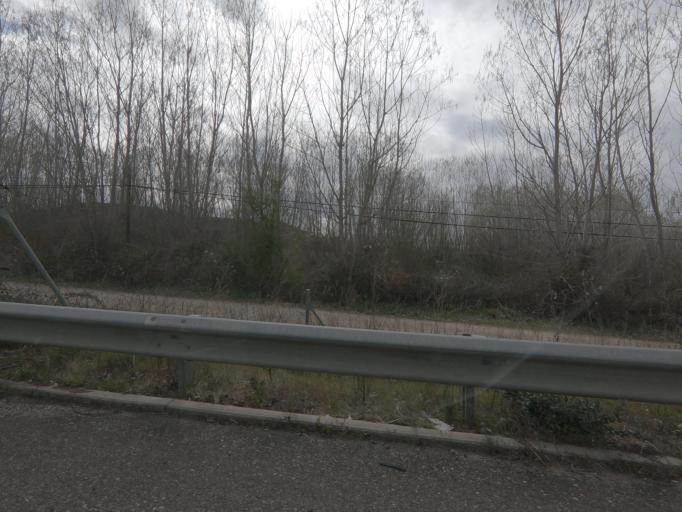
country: ES
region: Castille and Leon
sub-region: Provincia de Salamanca
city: Ciudad Rodrigo
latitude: 40.5827
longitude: -6.5375
